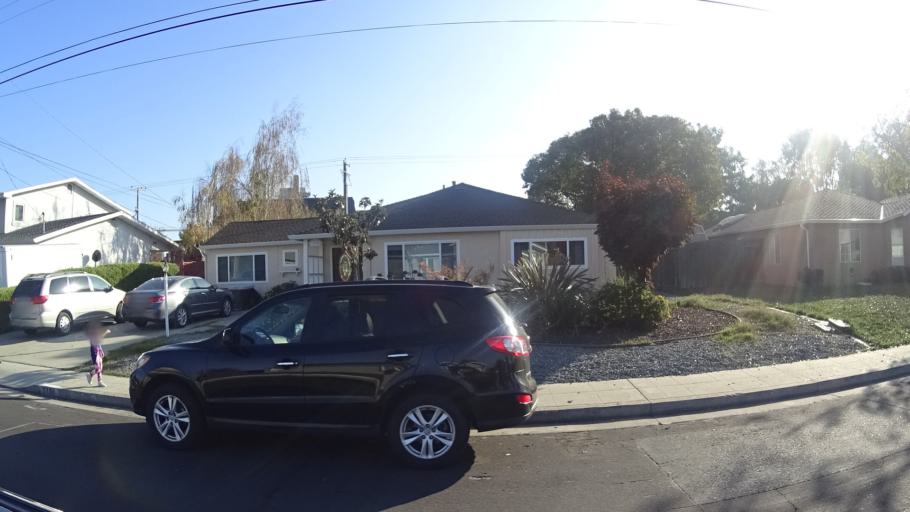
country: US
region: California
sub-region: Santa Clara County
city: Santa Clara
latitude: 37.3474
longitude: -121.9846
